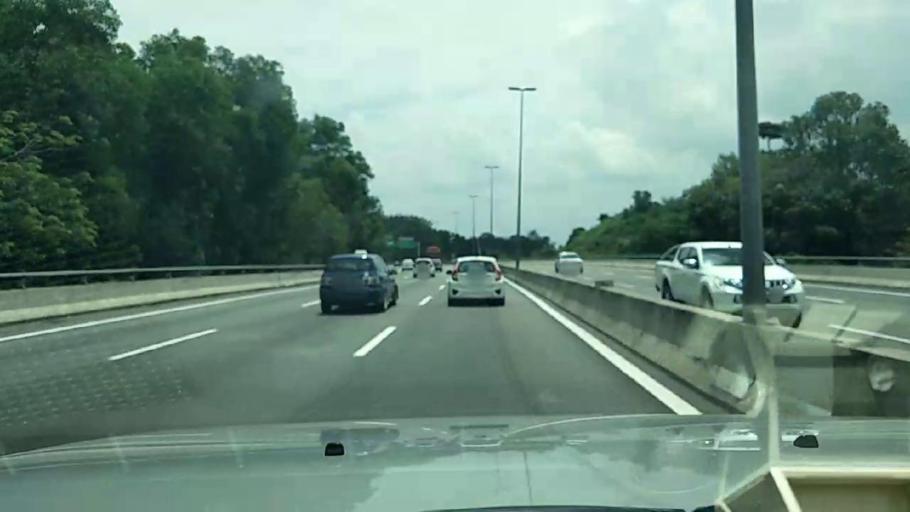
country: MY
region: Selangor
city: Kampong Baharu Balakong
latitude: 3.0565
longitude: 101.6885
